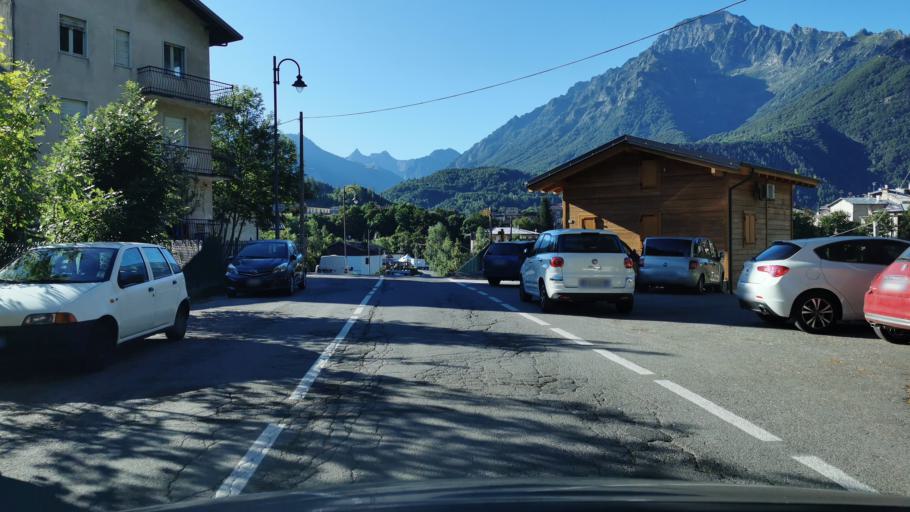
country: IT
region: Piedmont
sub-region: Provincia di Cuneo
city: Entracque
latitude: 44.2411
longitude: 7.3959
